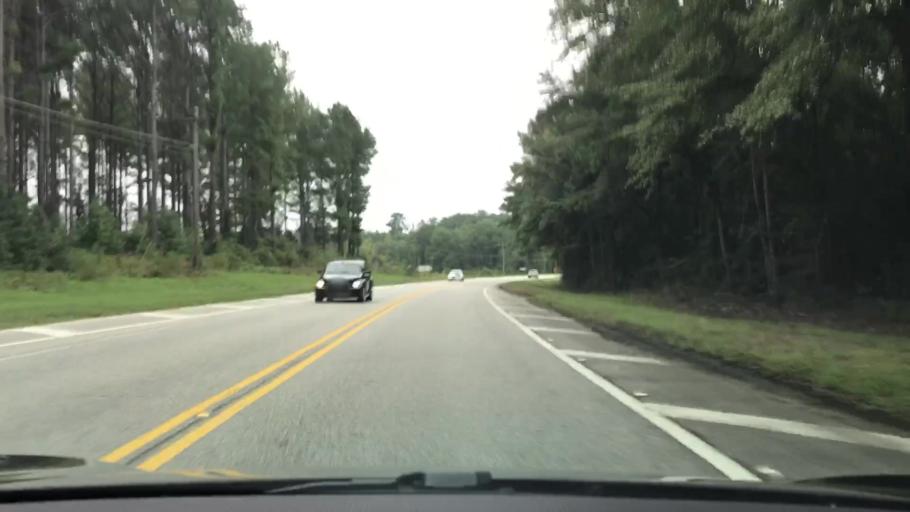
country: US
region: Alabama
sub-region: Coffee County
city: Elba
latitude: 31.4587
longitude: -86.0692
